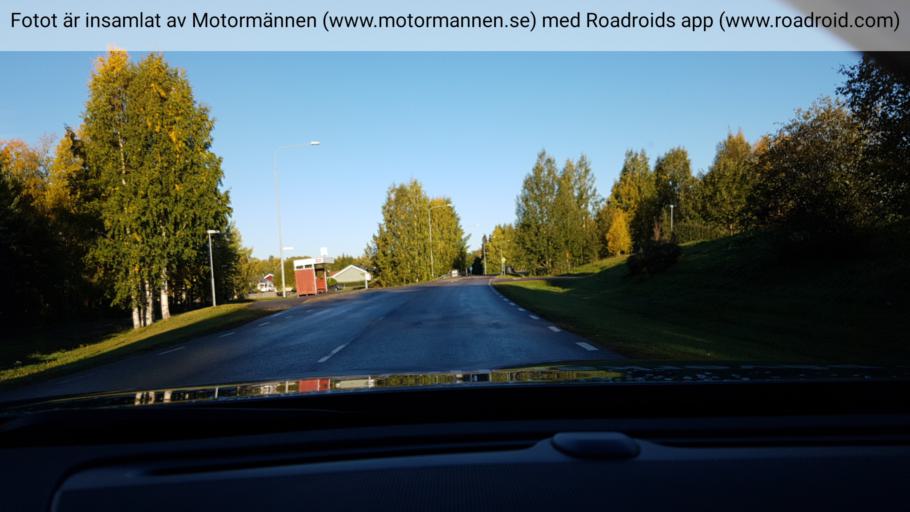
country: SE
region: Norrbotten
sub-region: Lulea Kommun
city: Sodra Sunderbyn
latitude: 65.6512
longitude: 21.9543
